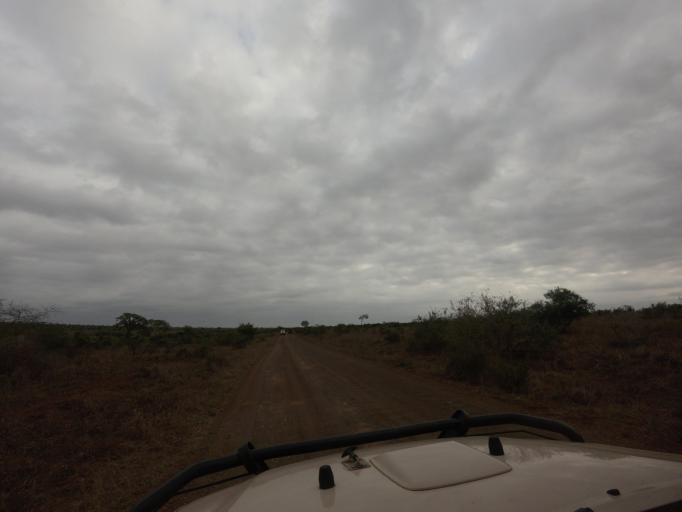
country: ZA
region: Mpumalanga
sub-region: Ehlanzeni District
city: Komatipoort
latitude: -25.3250
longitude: 31.9061
